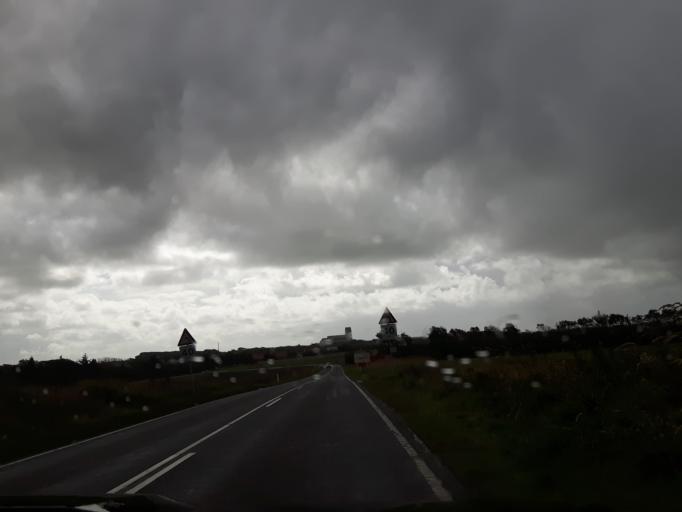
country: DK
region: North Denmark
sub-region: Thisted Kommune
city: Hurup
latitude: 56.7840
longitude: 8.3233
